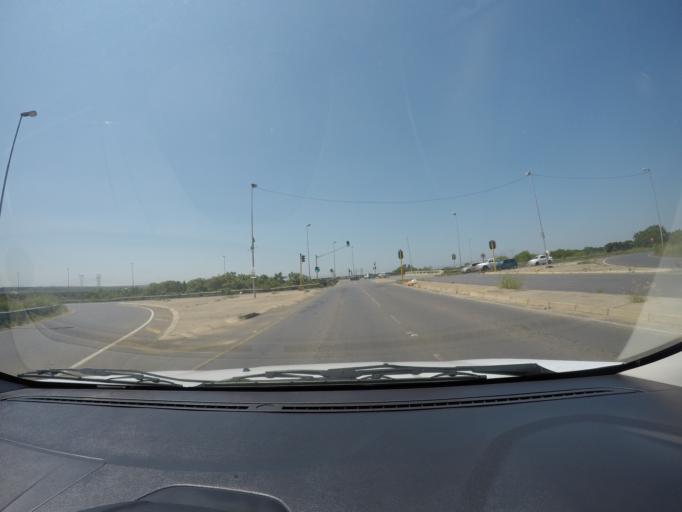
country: ZA
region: KwaZulu-Natal
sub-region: uThungulu District Municipality
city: Empangeni
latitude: -28.7761
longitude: 31.9584
